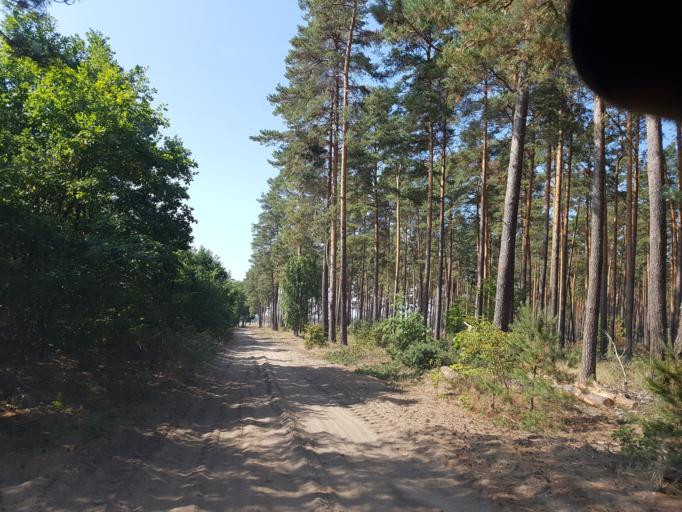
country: DE
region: Brandenburg
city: Gorzke
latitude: 52.0739
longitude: 12.3298
